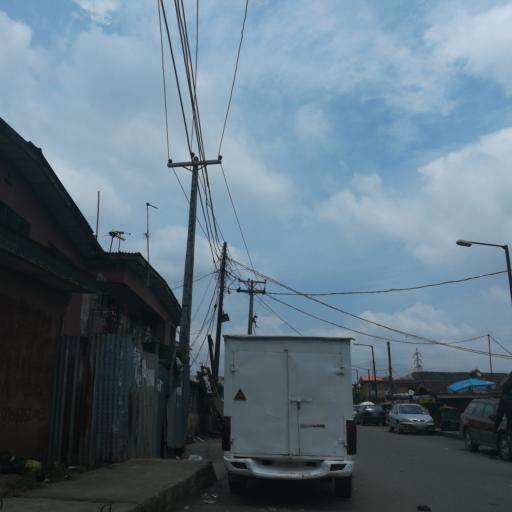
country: NG
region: Lagos
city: Ojota
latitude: 6.5857
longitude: 3.3821
